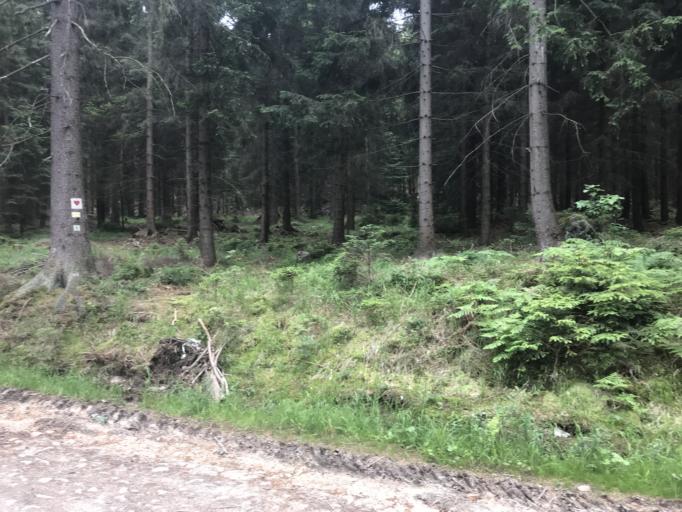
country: PL
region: Lower Silesian Voivodeship
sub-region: Powiat klodzki
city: Polanica-Zdroj
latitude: 50.3697
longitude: 16.4998
